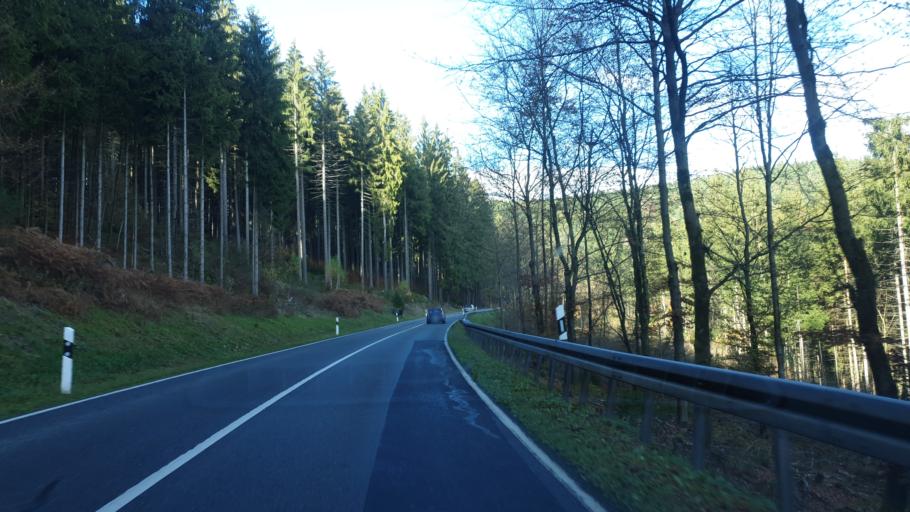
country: DE
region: Saxony
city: Bockau
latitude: 50.5525
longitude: 12.6792
